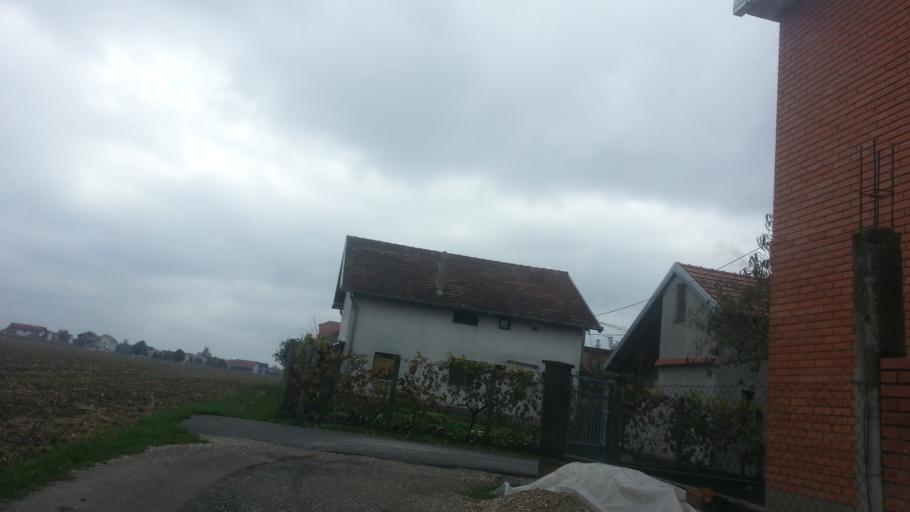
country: RS
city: Novi Banovci
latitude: 44.9183
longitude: 20.2828
